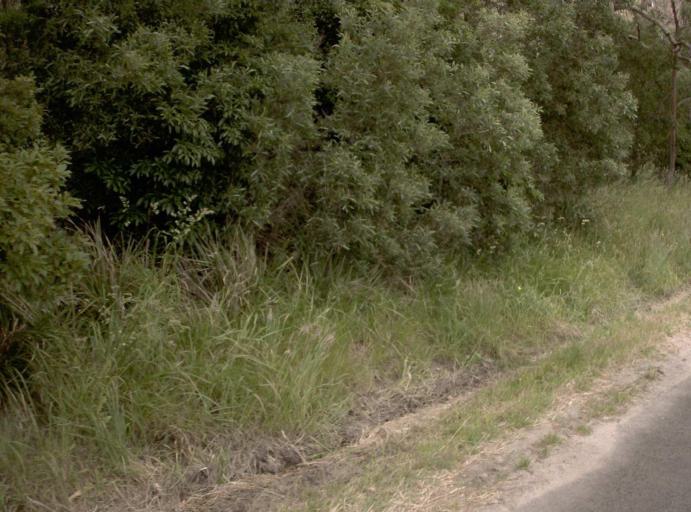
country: AU
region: Victoria
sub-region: Baw Baw
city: Warragul
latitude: -38.4073
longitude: 146.0548
